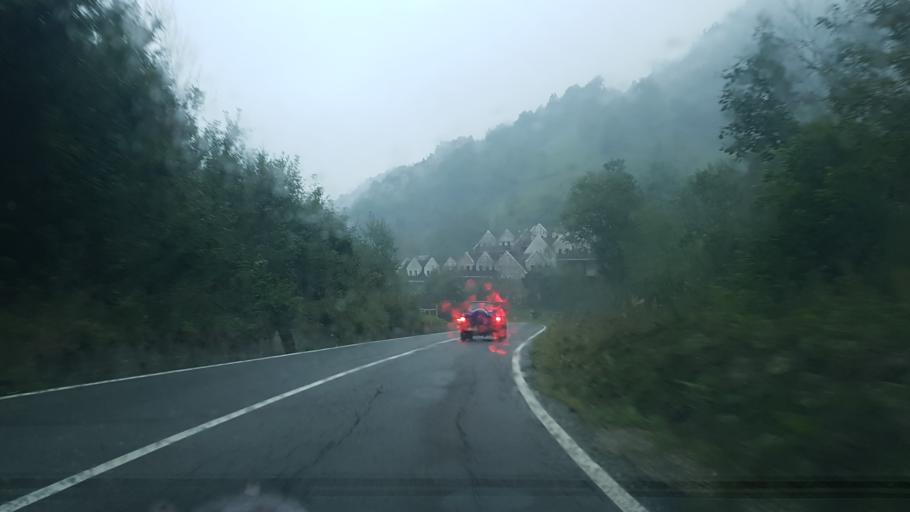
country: IT
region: Piedmont
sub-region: Provincia di Cuneo
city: Frabosa Soprana
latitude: 44.2625
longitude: 7.7652
